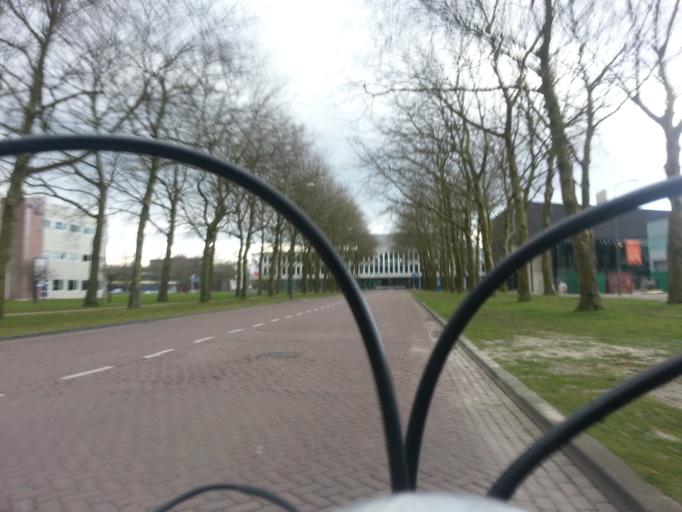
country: NL
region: North Brabant
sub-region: Gemeente Eindhoven
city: Villapark
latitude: 51.4484
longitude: 5.4914
